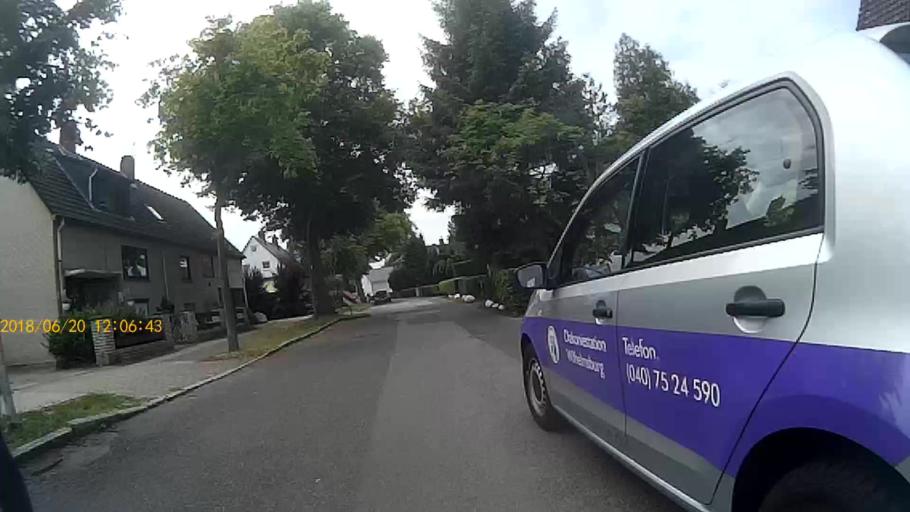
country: DE
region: Hamburg
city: Harburg
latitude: 53.4894
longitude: 10.0092
